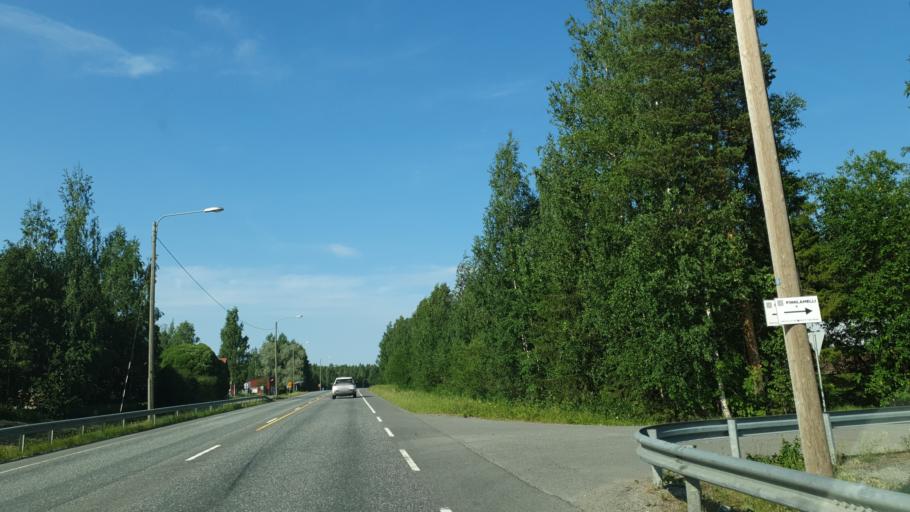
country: FI
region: Northern Savo
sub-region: Kuopio
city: Siilinjaervi
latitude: 63.1261
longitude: 27.7718
